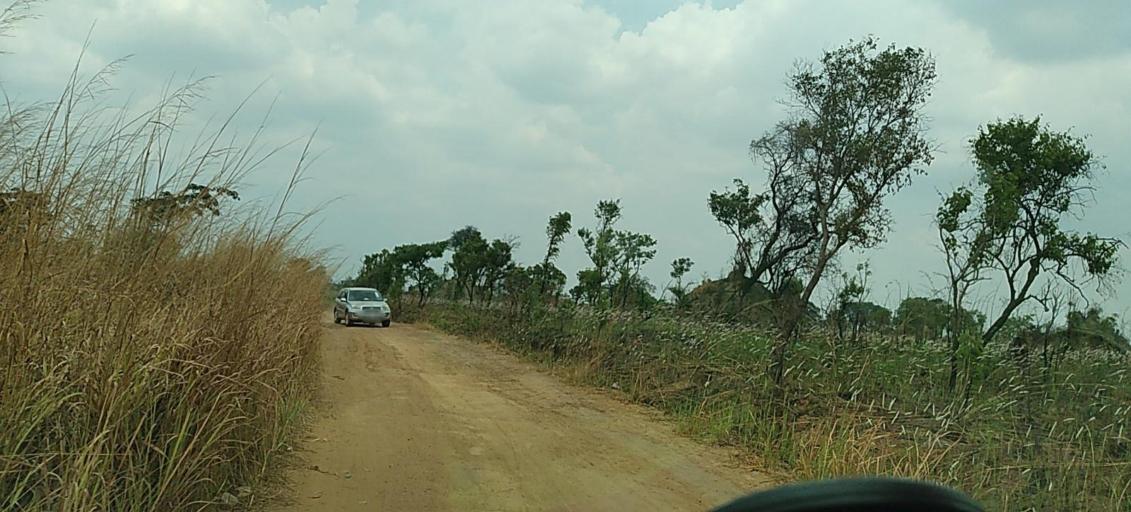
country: ZM
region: North-Western
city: Kansanshi
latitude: -12.0838
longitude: 26.3661
